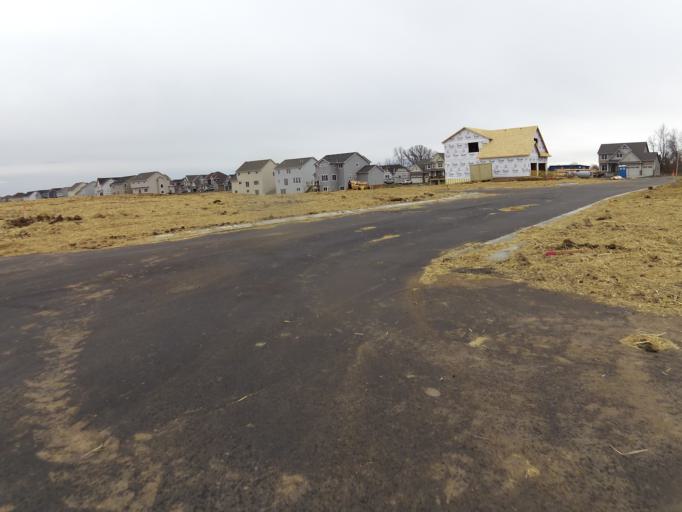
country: US
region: Minnesota
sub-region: Washington County
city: Lake Elmo
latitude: 44.9978
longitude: -92.8707
